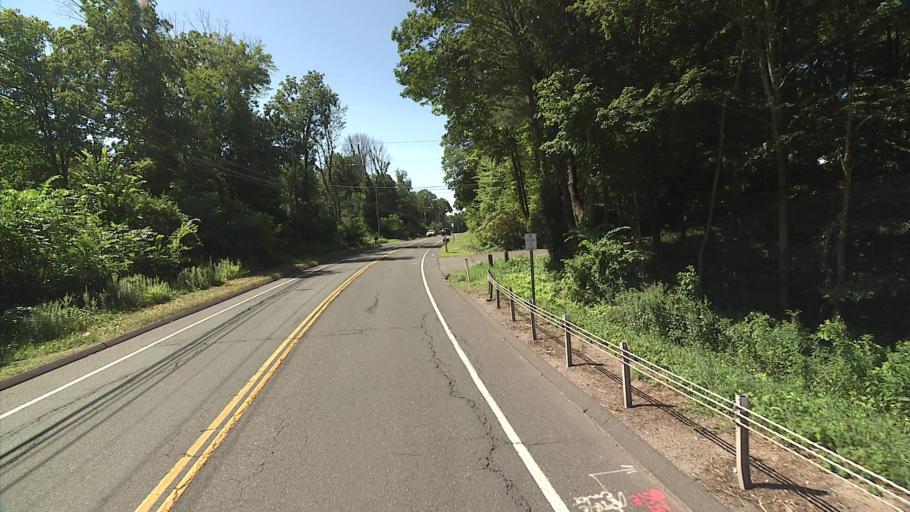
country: US
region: Connecticut
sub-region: Hartford County
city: Weatogue
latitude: 41.7913
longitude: -72.8155
